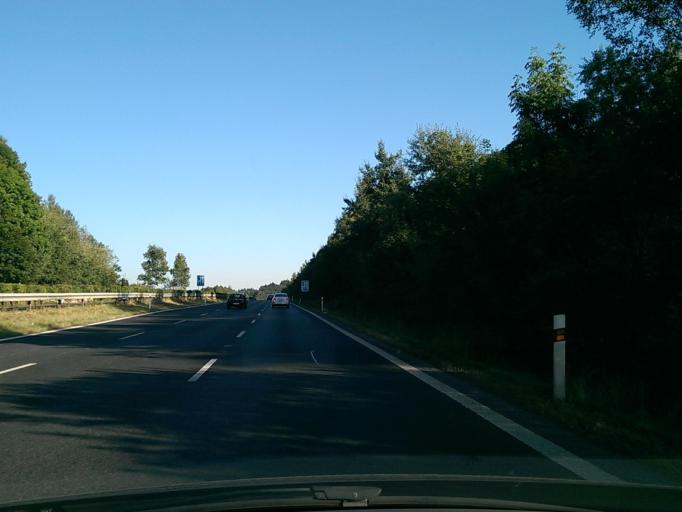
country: CZ
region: Liberecky
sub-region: Okres Liberec
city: Liberec
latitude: 50.7234
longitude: 15.0628
